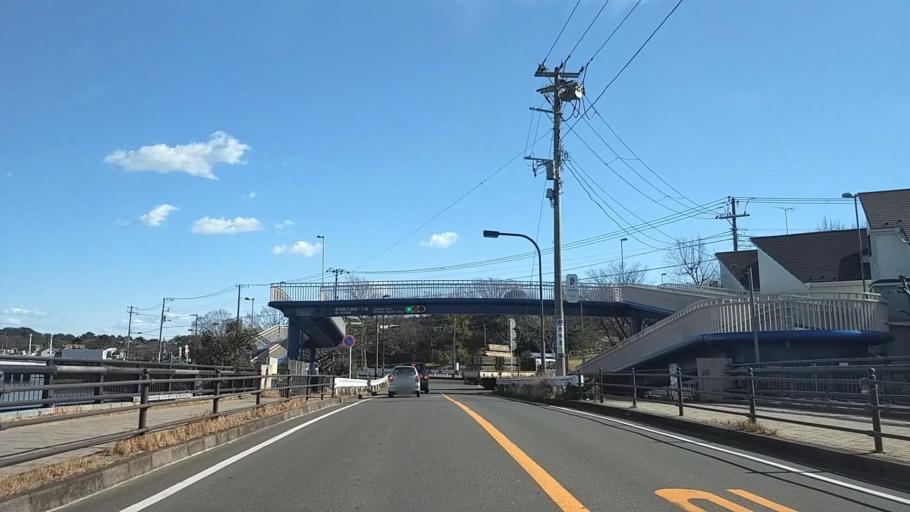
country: JP
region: Kanagawa
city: Yokosuka
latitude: 35.3261
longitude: 139.6291
